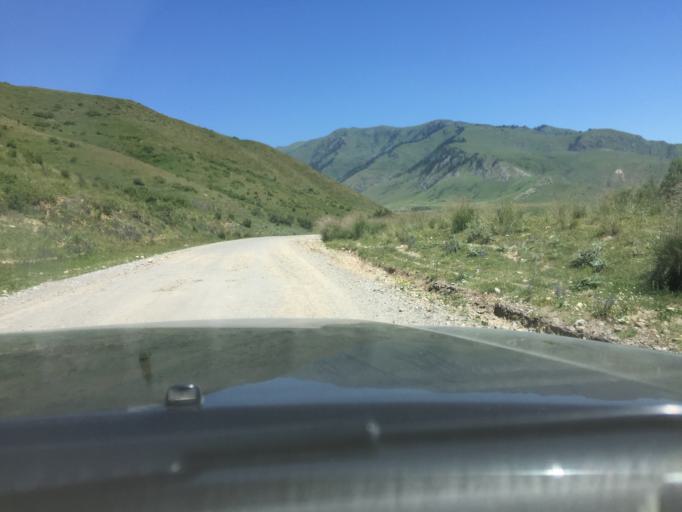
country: KG
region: Ysyk-Koel
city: Teploklyuchenka
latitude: 42.7291
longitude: 78.8226
